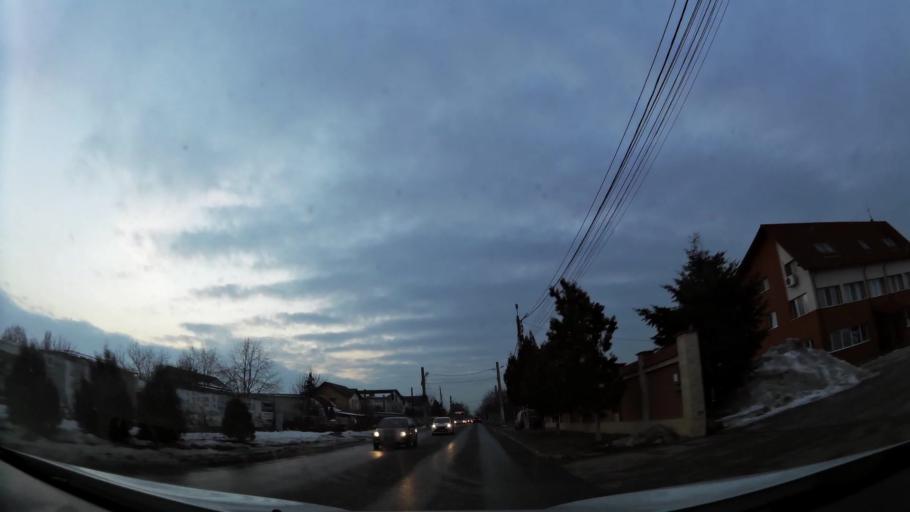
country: RO
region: Ilfov
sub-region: Comuna Popesti-Leordeni
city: Popesti-Leordeni
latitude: 44.3807
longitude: 26.1817
